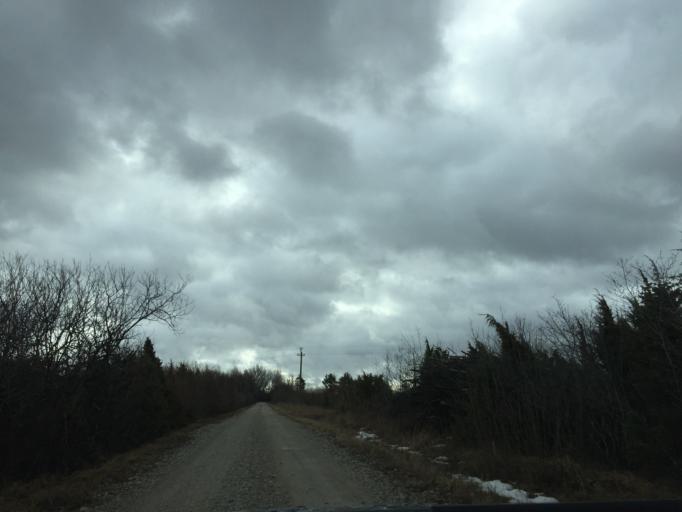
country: EE
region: Laeaene
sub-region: Haapsalu linn
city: Haapsalu
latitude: 58.6848
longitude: 23.5085
